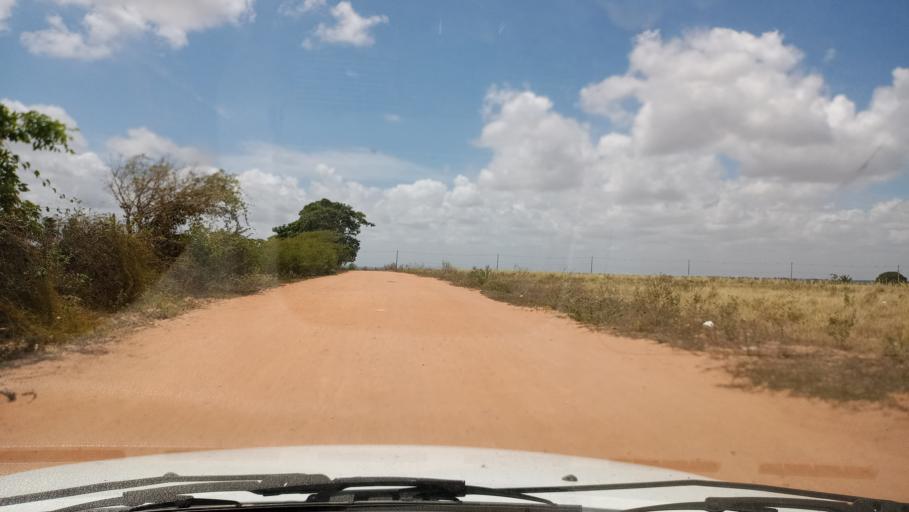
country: BR
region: Rio Grande do Norte
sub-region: Goianinha
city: Goianinha
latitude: -6.2840
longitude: -35.2865
